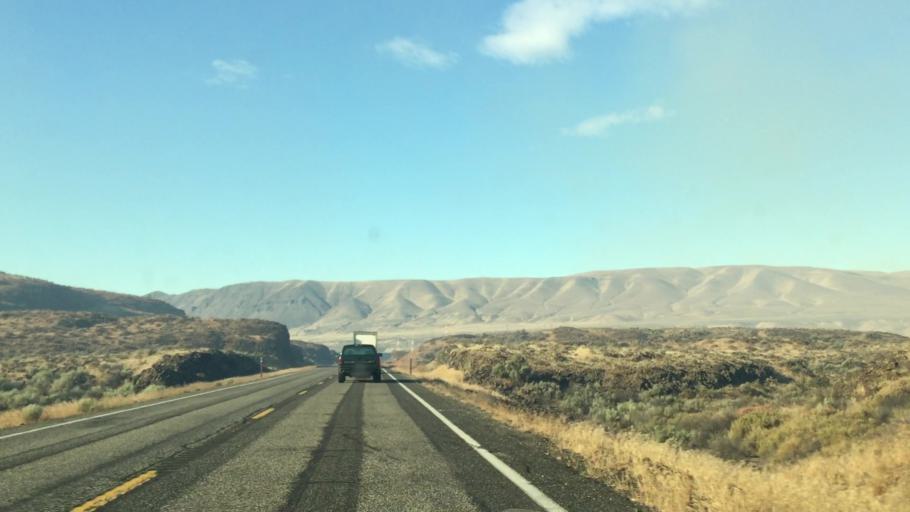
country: US
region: Washington
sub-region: Grant County
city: Mattawa
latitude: 46.8994
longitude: -119.9511
